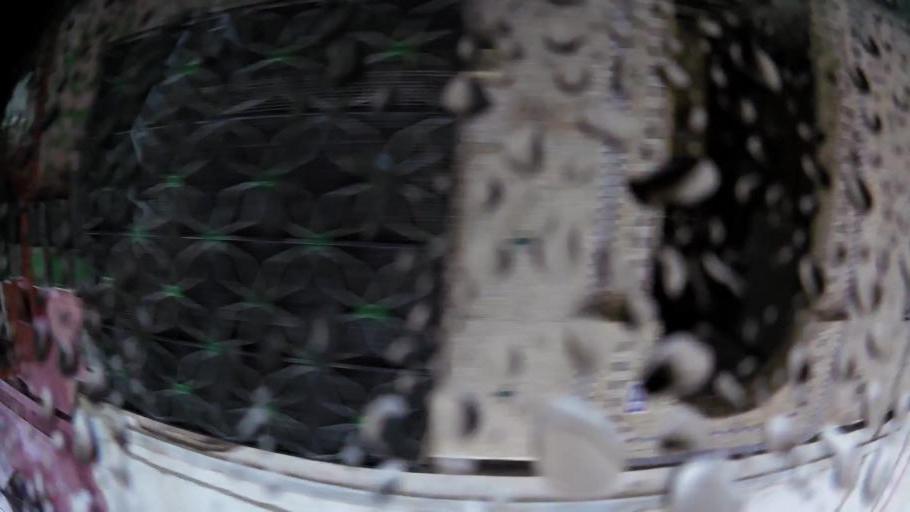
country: MA
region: Grand Casablanca
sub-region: Mediouna
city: Tit Mellil
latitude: 33.5681
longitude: -7.5297
